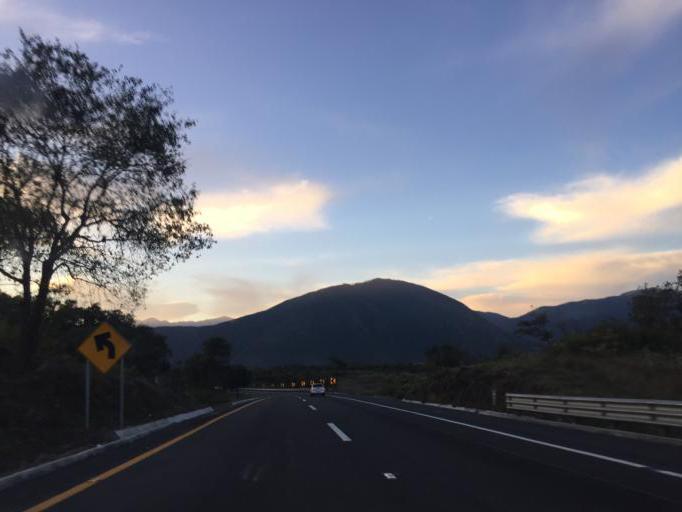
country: MX
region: Veracruz
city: Maltrata
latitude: 18.8386
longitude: -97.2620
